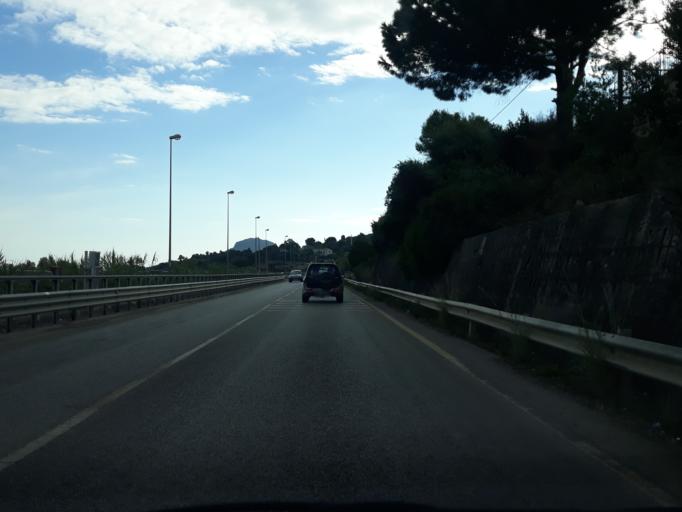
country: IT
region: Sicily
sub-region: Palermo
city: Cefalu
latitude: 38.0259
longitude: 13.9805
